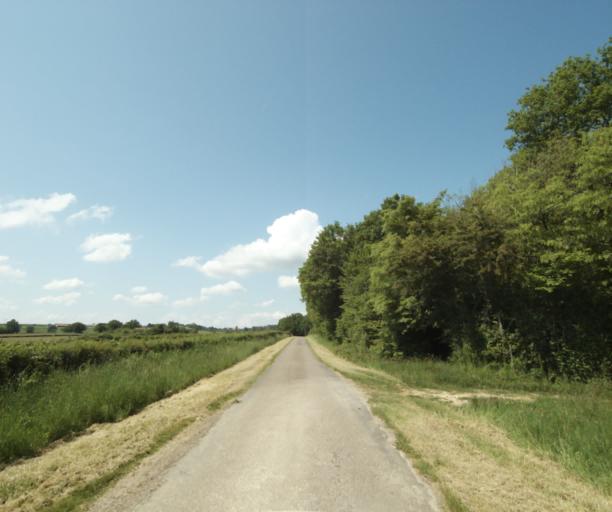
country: FR
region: Bourgogne
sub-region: Departement de Saone-et-Loire
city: Perrecy-les-Forges
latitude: 46.5885
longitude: 4.1597
